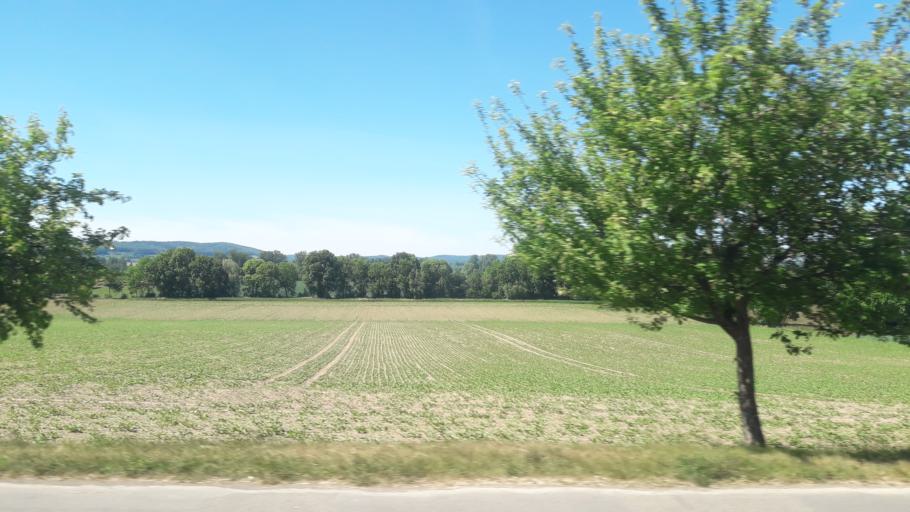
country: DE
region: North Rhine-Westphalia
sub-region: Regierungsbezirk Detmold
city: Steinheim
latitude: 51.8365
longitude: 9.0622
